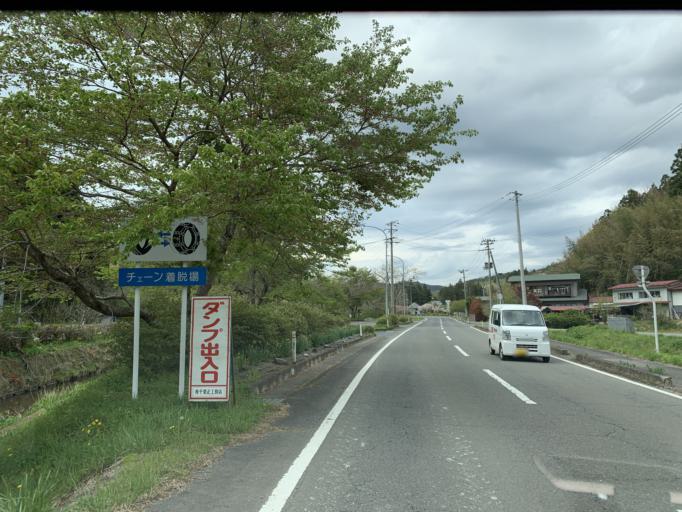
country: JP
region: Iwate
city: Ichinoseki
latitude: 38.7833
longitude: 141.3260
